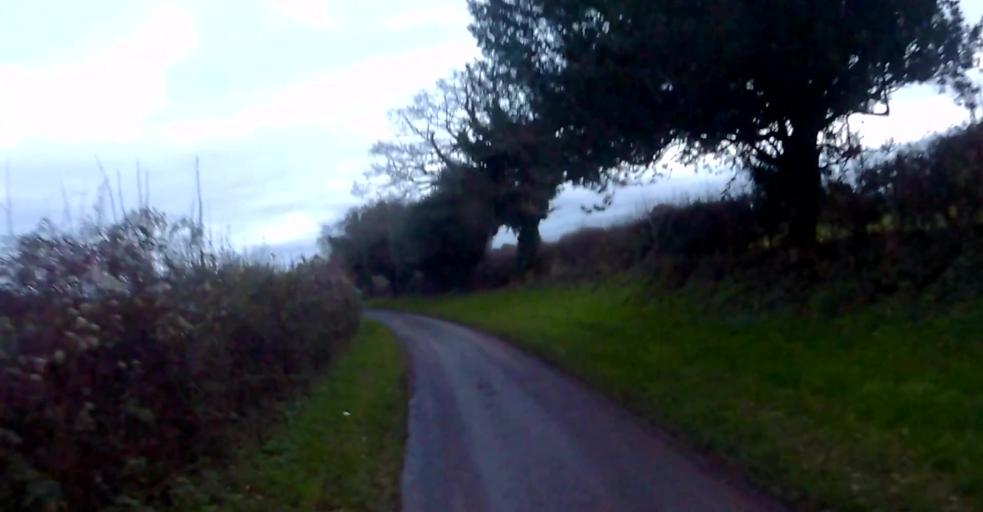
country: GB
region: England
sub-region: Hampshire
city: Overton
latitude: 51.2562
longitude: -1.2110
